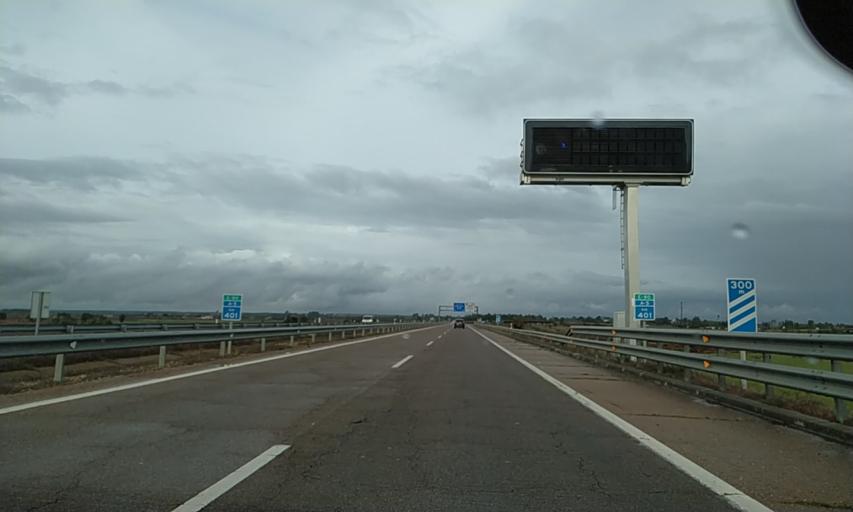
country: ES
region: Extremadura
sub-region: Provincia de Badajoz
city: Badajoz
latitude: 38.9182
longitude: -6.9753
